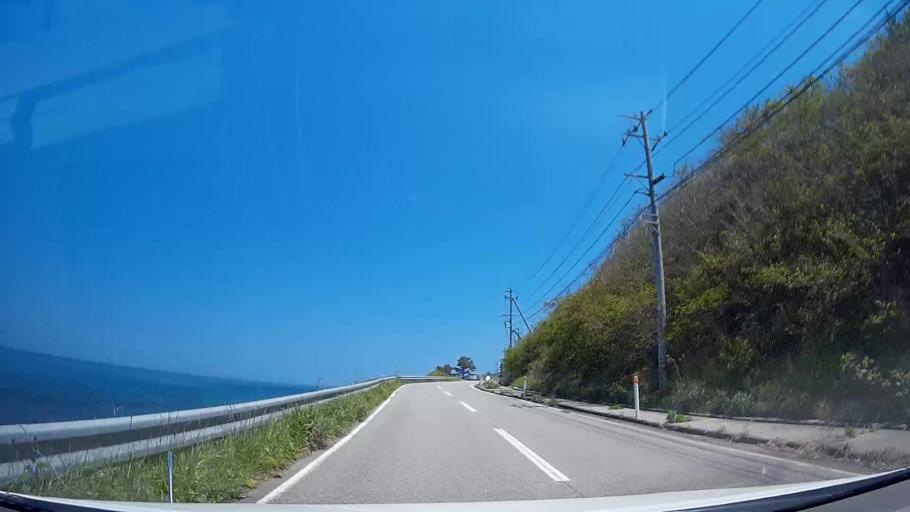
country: JP
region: Ishikawa
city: Nanao
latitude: 37.4377
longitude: 137.0370
